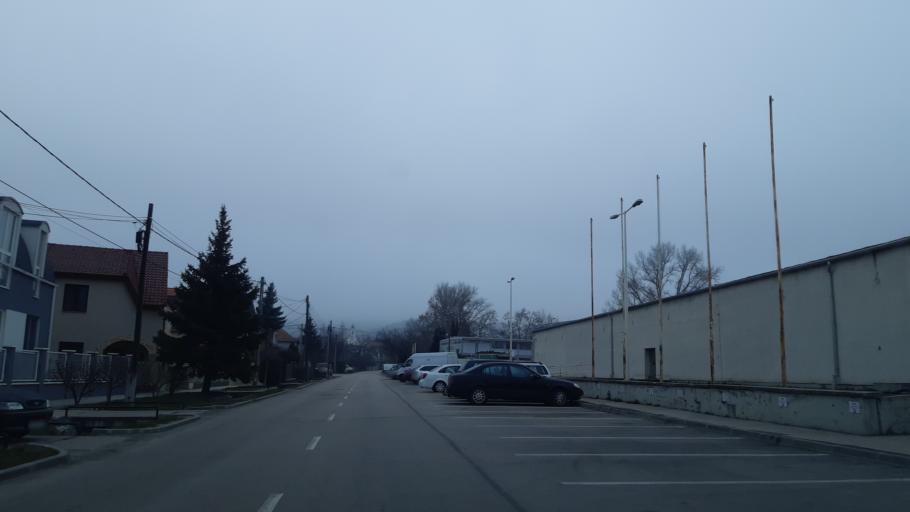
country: HU
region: Pest
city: Budaors
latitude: 47.4540
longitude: 18.9636
